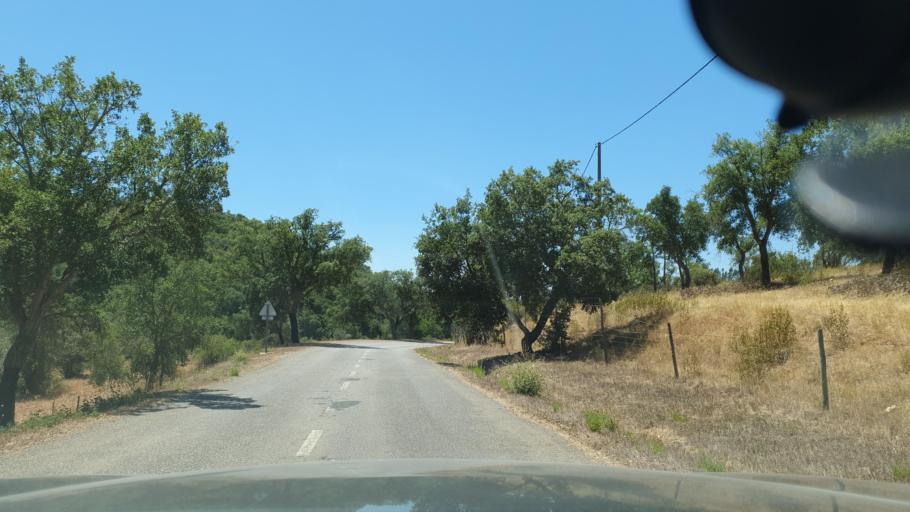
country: PT
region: Beja
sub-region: Odemira
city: Odemira
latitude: 37.6133
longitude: -8.5055
